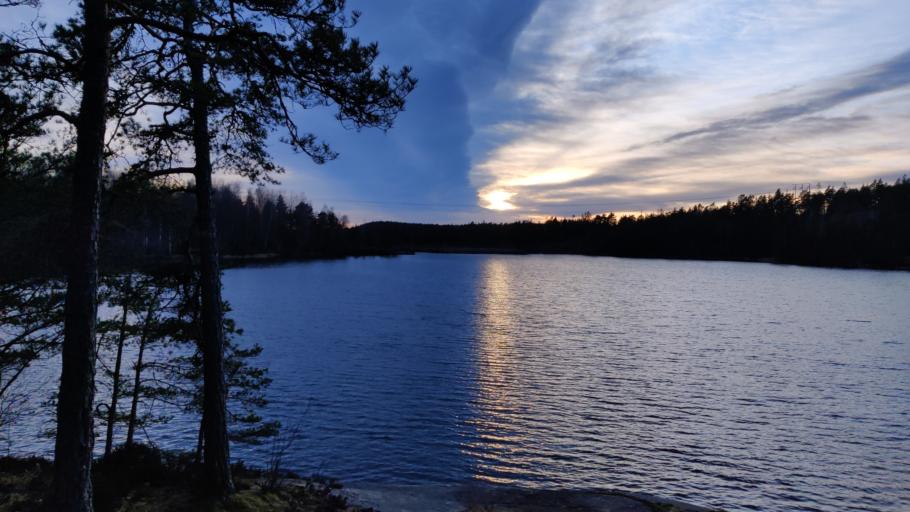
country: SE
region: Vaestra Goetaland
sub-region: Uddevalla Kommun
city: Uddevalla
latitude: 58.3610
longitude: 12.0146
